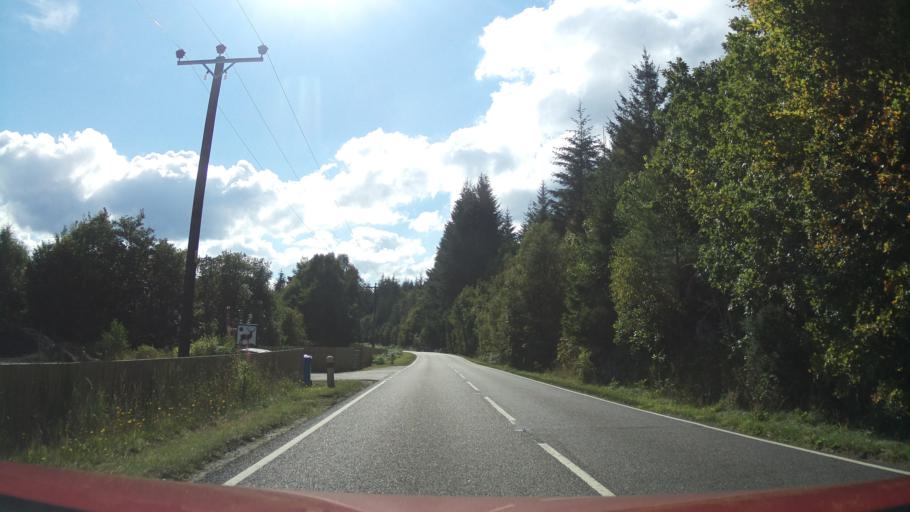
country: GB
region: Scotland
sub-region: Highland
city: Spean Bridge
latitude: 57.1581
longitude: -4.6661
